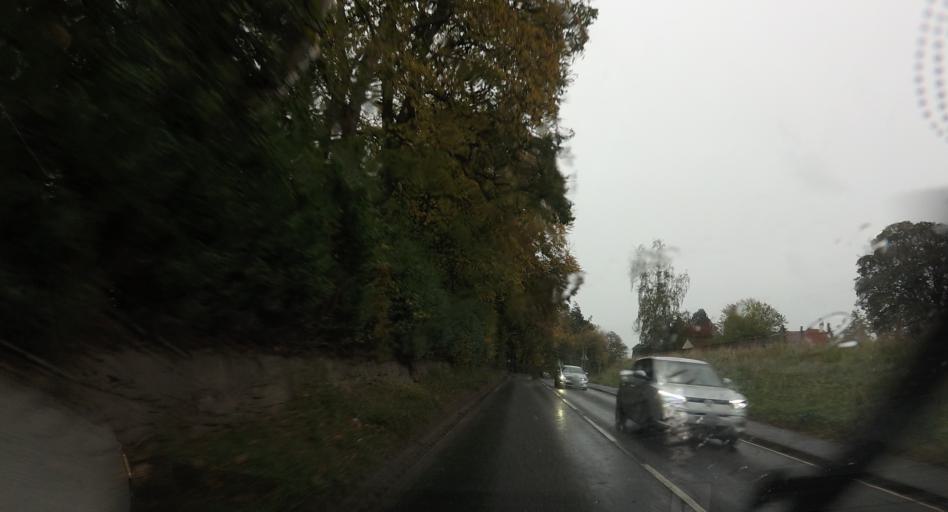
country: GB
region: Scotland
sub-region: Perth and Kinross
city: Coupar Angus
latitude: 56.5497
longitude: -3.2700
